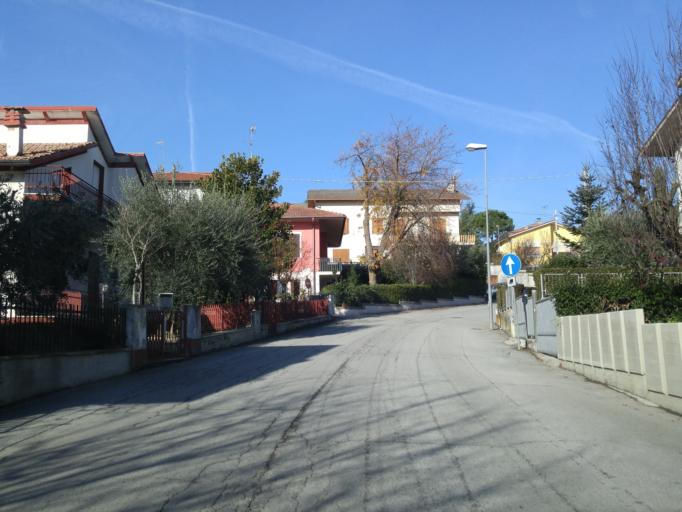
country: IT
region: The Marches
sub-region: Provincia di Pesaro e Urbino
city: Lucrezia
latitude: 43.7754
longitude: 12.9355
